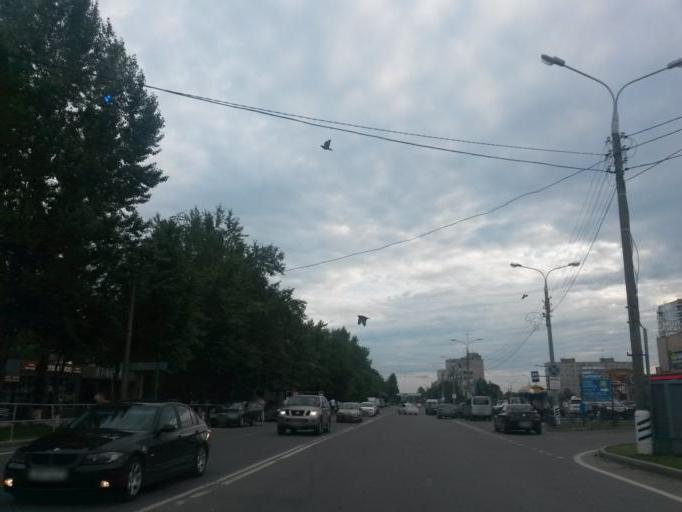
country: RU
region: Moskovskaya
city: Vostryakovo
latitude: 55.4167
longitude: 37.8367
